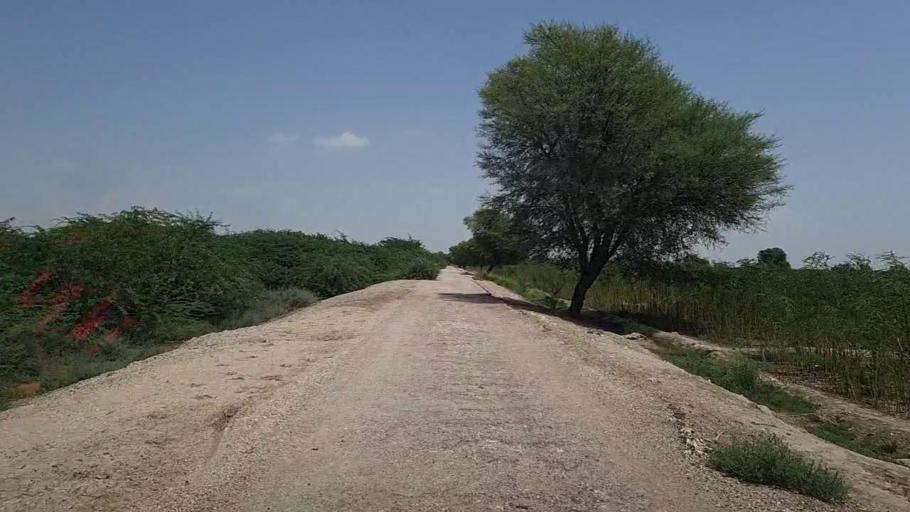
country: PK
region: Sindh
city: Pad Idan
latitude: 26.7444
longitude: 68.3007
